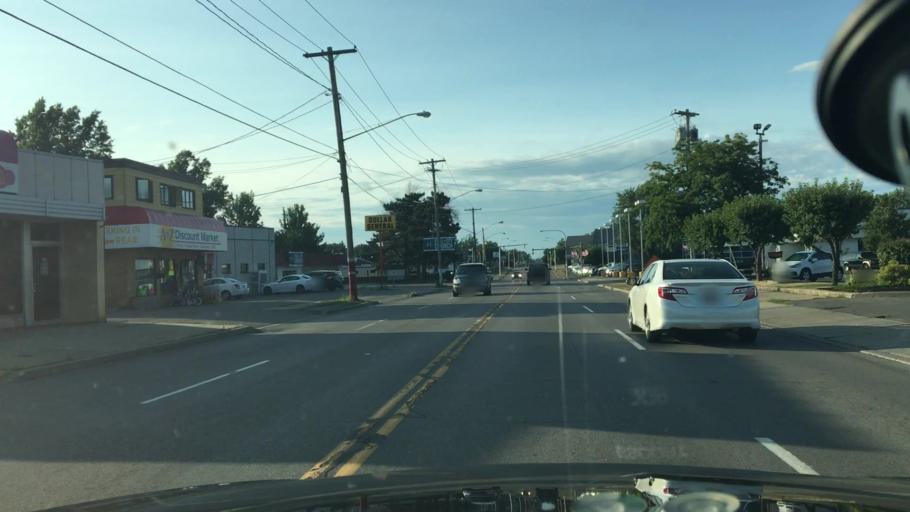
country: US
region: New York
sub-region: Erie County
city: Lackawanna
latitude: 42.8306
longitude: -78.8052
